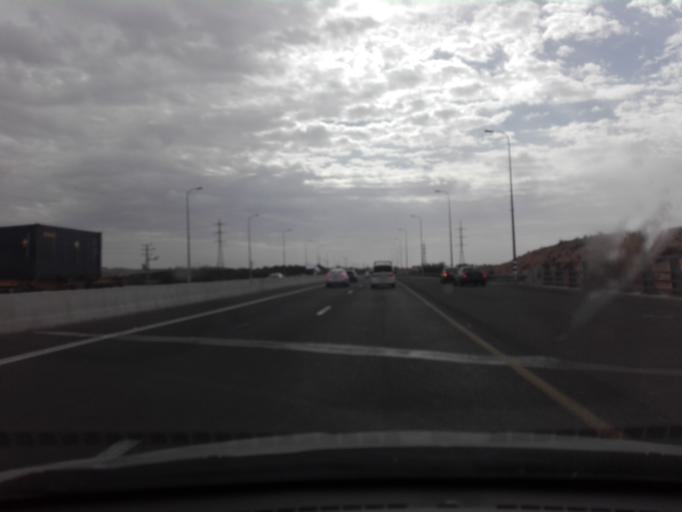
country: IL
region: Southern District
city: Lehavim
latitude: 31.3248
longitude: 34.7865
